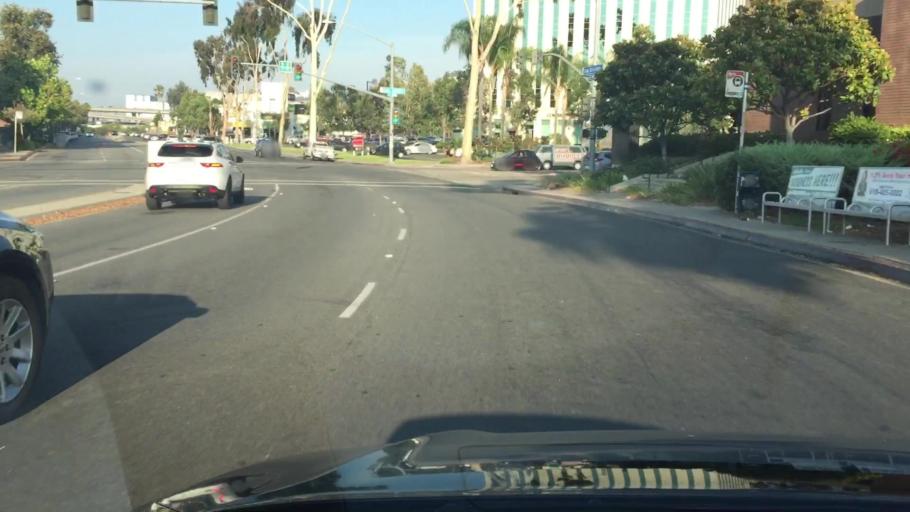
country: US
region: California
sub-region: San Diego County
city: San Diego
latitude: 32.7708
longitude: -117.1447
